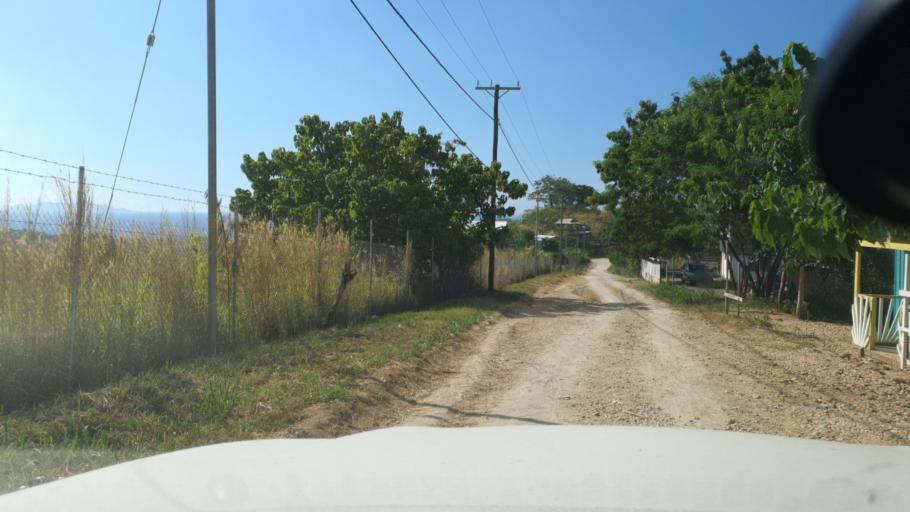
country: SB
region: Guadalcanal
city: Honiara
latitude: -9.4610
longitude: 159.9757
